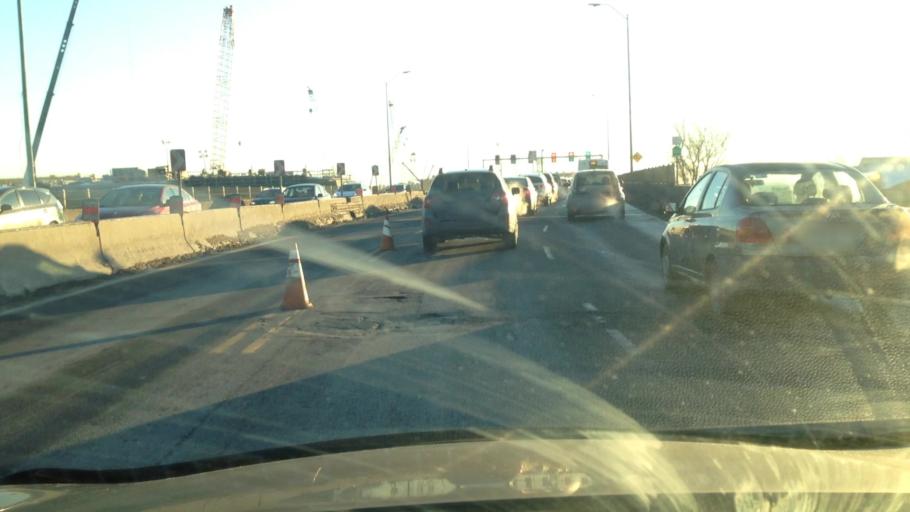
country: CA
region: Quebec
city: Westmount
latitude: 45.4699
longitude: -73.5367
